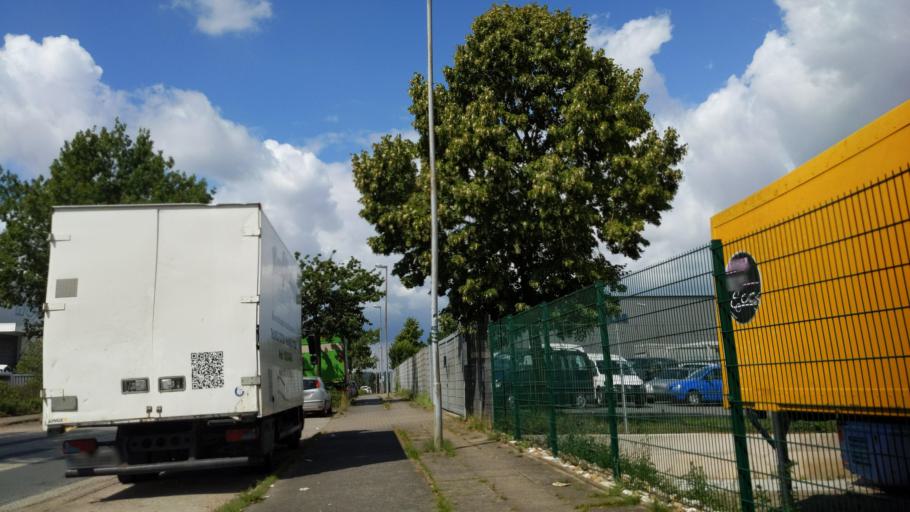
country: DE
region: Schleswig-Holstein
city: Reinfeld
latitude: 53.8292
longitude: 10.5027
